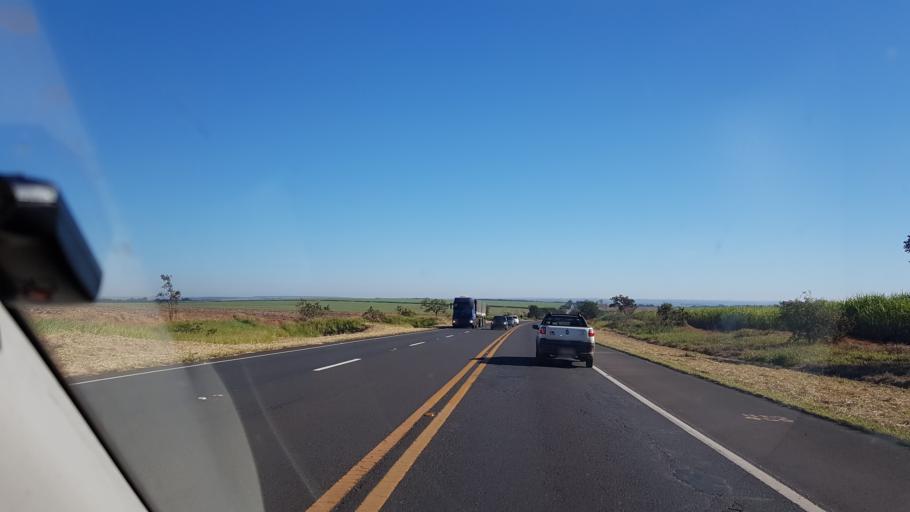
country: BR
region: Sao Paulo
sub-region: Assis
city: Assis
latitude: -22.5662
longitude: -50.5227
